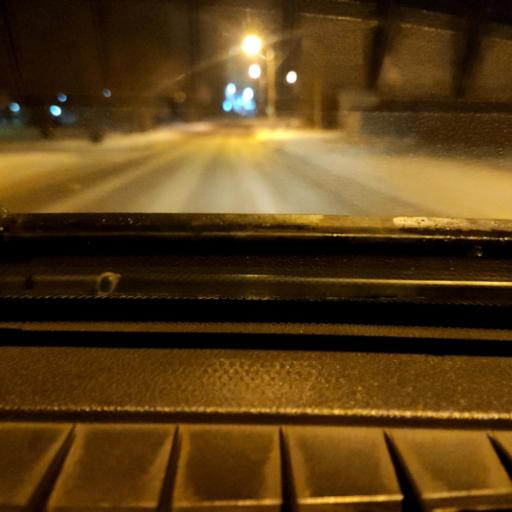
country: RU
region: Perm
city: Perm
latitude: 58.0882
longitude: 56.4067
